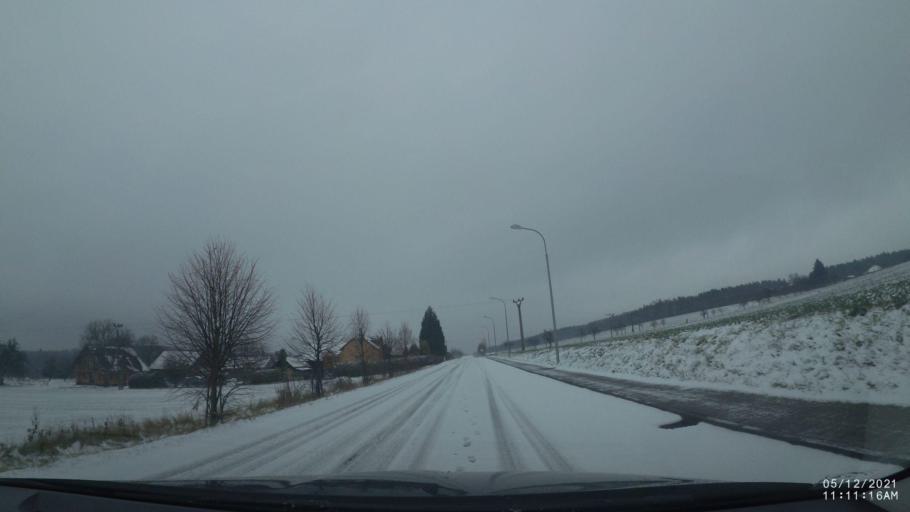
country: CZ
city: Solnice
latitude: 50.1822
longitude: 16.2232
